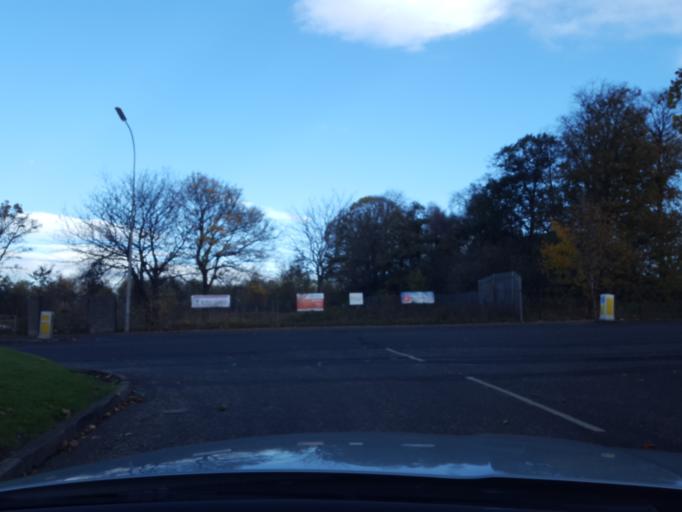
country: GB
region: Scotland
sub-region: North Lanarkshire
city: Chryston
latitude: 55.8690
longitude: -4.1203
